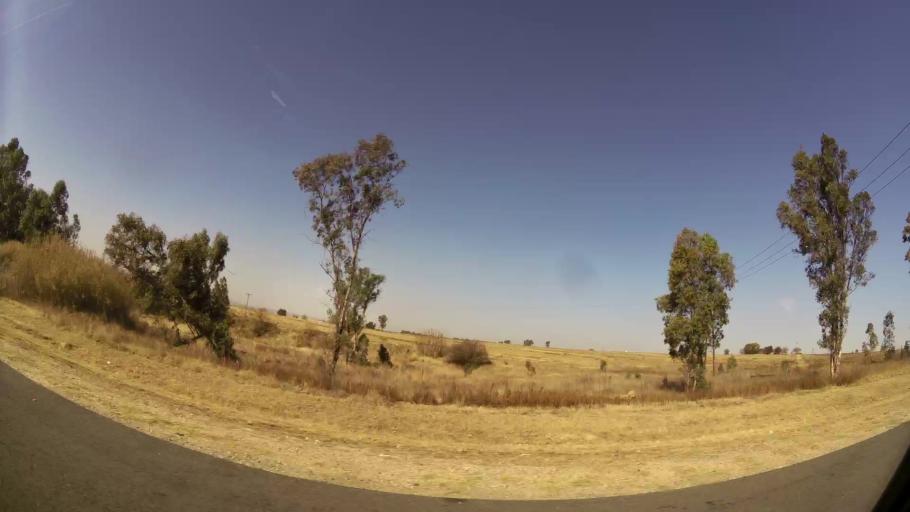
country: ZA
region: Gauteng
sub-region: City of Johannesburg Metropolitan Municipality
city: Diepsloot
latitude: -25.9542
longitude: 27.9544
